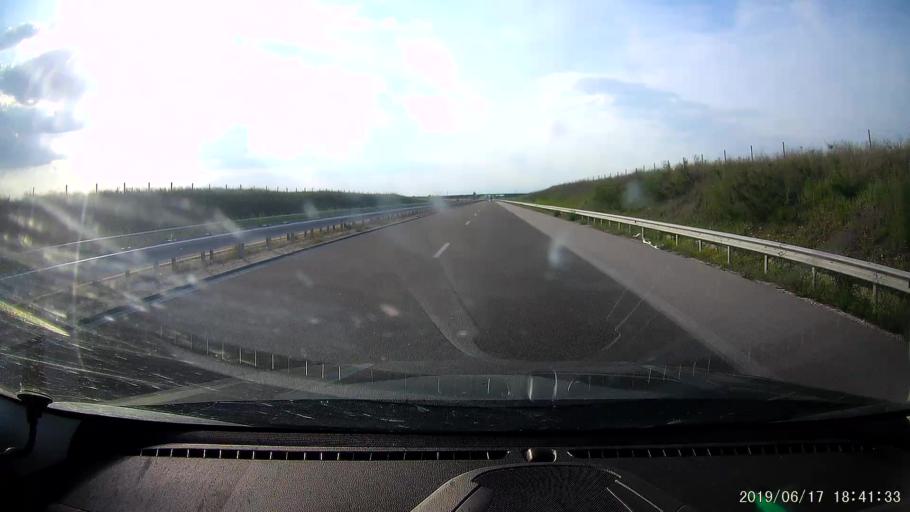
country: BG
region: Stara Zagora
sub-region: Obshtina Chirpan
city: Chirpan
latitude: 42.1744
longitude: 25.2537
